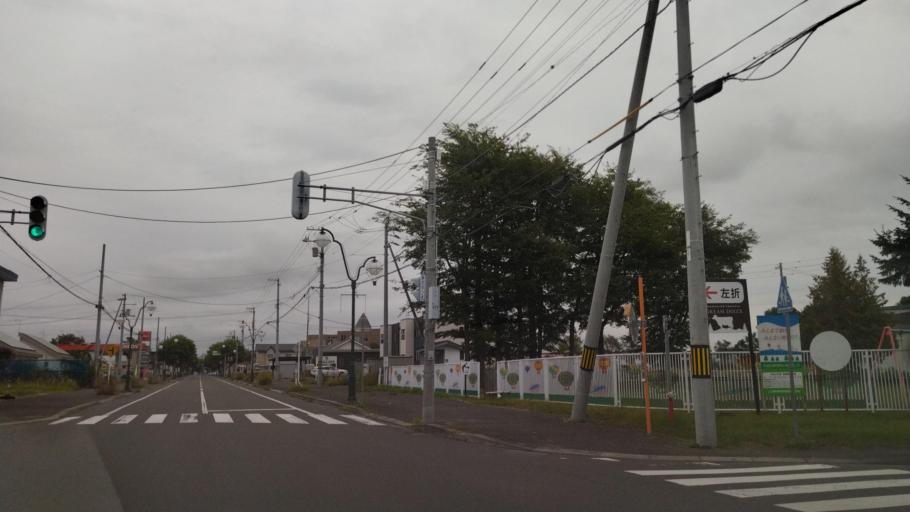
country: JP
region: Hokkaido
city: Otofuke
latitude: 43.2325
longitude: 143.2879
